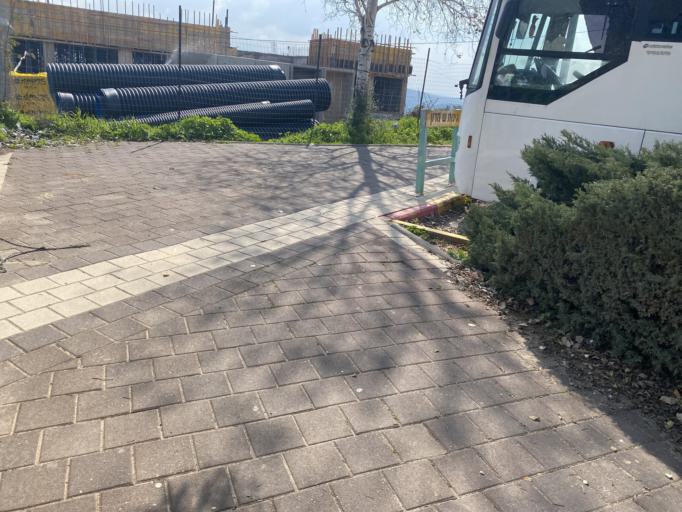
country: PS
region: West Bank
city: Karney Shomron
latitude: 32.1741
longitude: 35.0916
